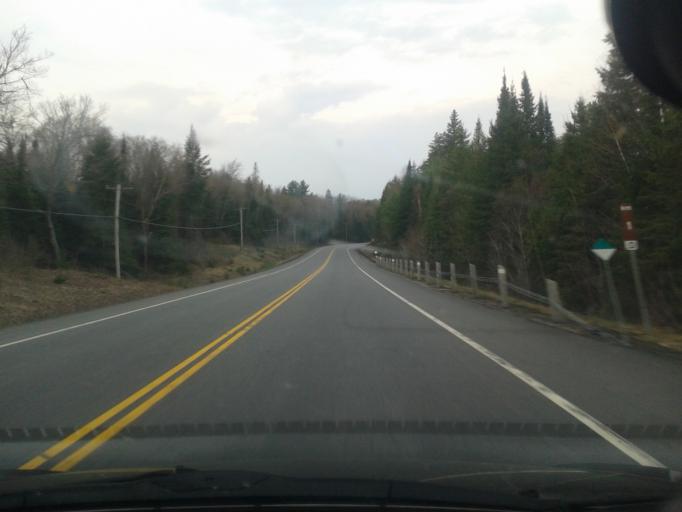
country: CA
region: Ontario
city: Huntsville
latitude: 45.4499
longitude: -78.8148
